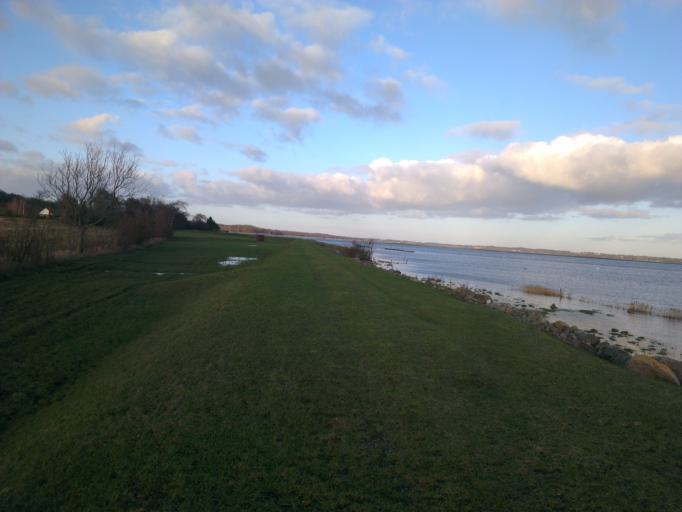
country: DK
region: Capital Region
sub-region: Frederikssund Kommune
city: Jaegerspris
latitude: 55.8661
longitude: 11.9985
